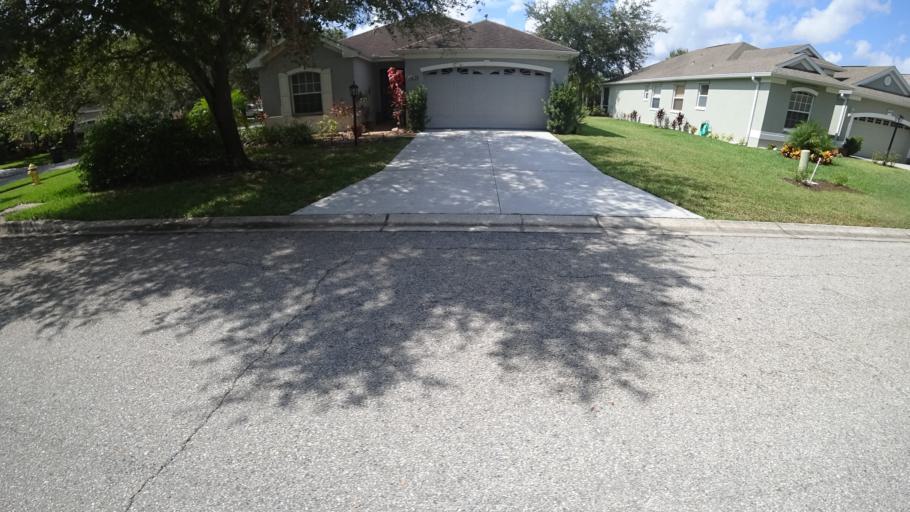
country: US
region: Florida
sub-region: Sarasota County
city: The Meadows
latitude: 27.4124
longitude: -82.4250
